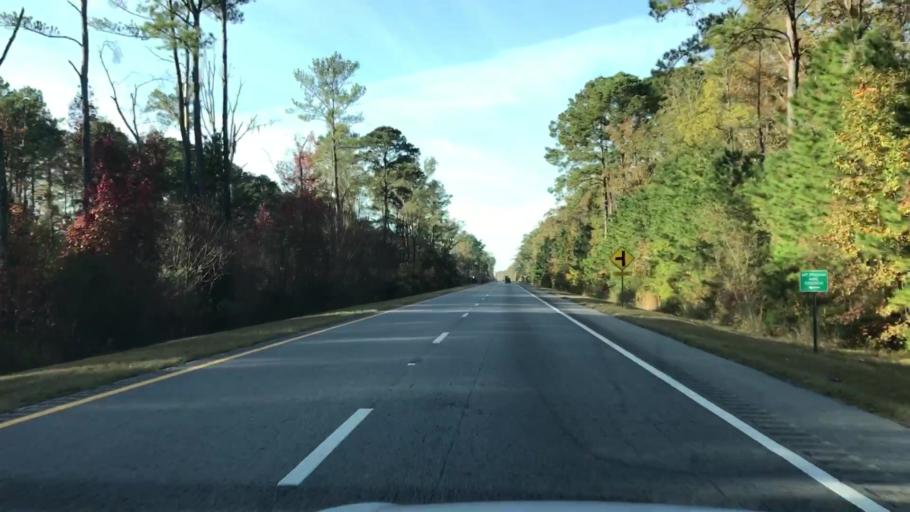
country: US
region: South Carolina
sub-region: Hampton County
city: Yemassee
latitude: 32.6345
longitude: -80.7192
